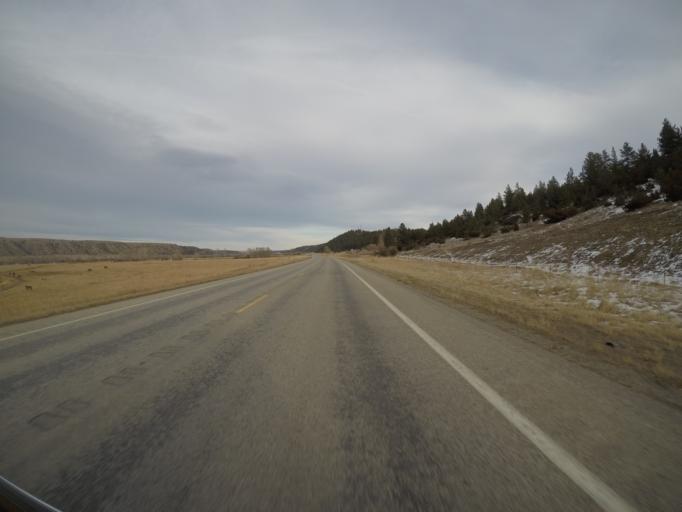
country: US
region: Montana
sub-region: Stillwater County
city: Absarokee
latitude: 45.5467
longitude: -109.3743
